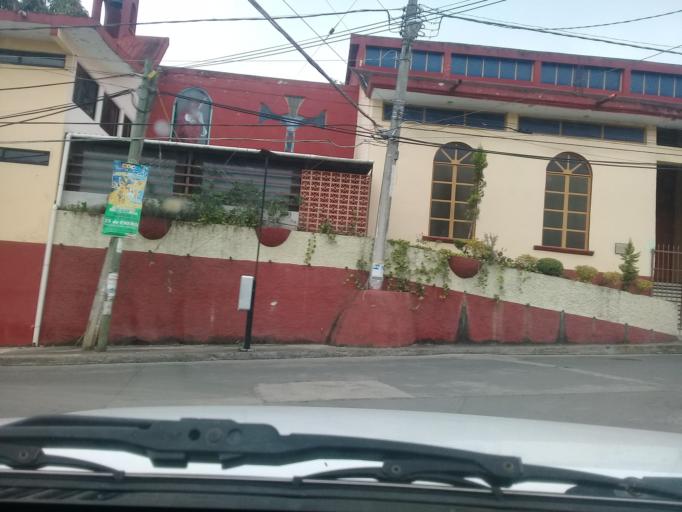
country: MX
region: Veracruz
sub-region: Xalapa
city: Xalapa de Enriquez
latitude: 19.5144
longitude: -96.9127
